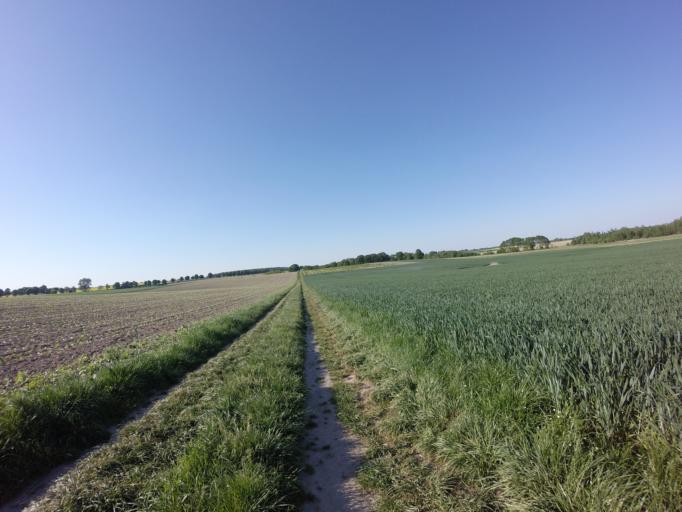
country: PL
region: West Pomeranian Voivodeship
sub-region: Powiat choszczenski
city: Choszczno
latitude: 53.1436
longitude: 15.3862
